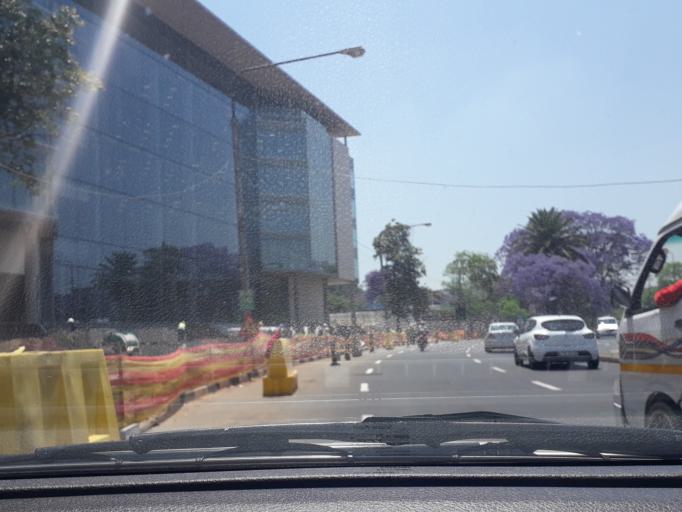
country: ZA
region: Gauteng
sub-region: City of Johannesburg Metropolitan Municipality
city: Johannesburg
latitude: -26.1420
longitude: 28.0435
